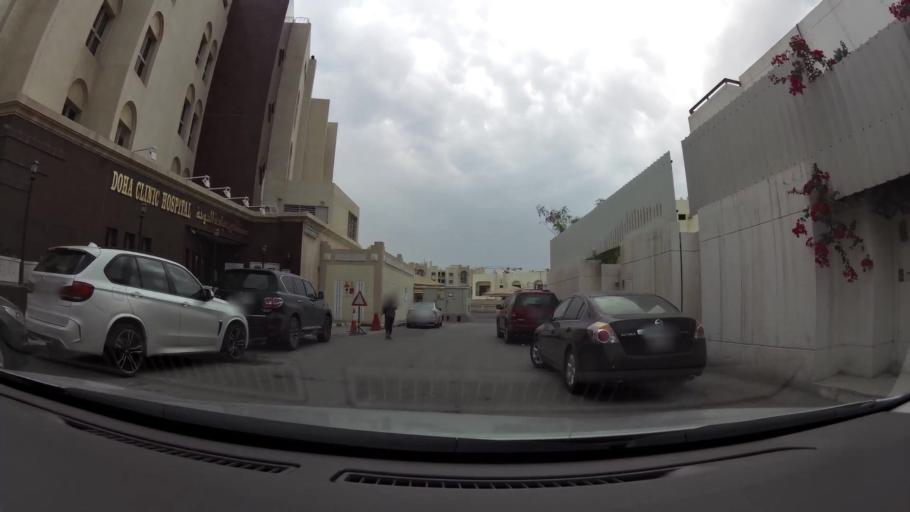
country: QA
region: Baladiyat ad Dawhah
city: Doha
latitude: 25.2744
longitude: 51.5034
